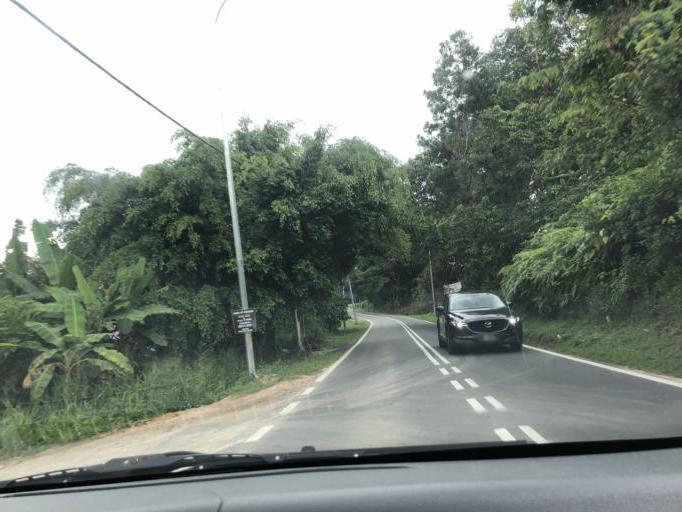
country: MY
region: Putrajaya
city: Putrajaya
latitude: 2.9197
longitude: 101.7494
